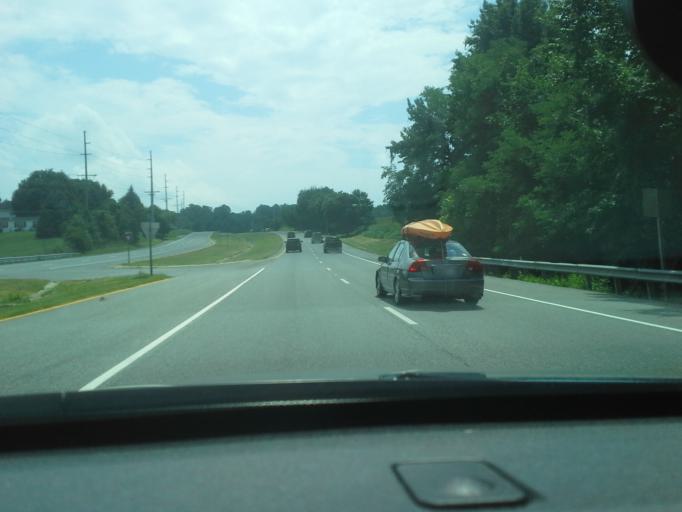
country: US
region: Maryland
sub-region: Calvert County
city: Dunkirk Town Center
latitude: 38.6878
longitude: -76.6375
